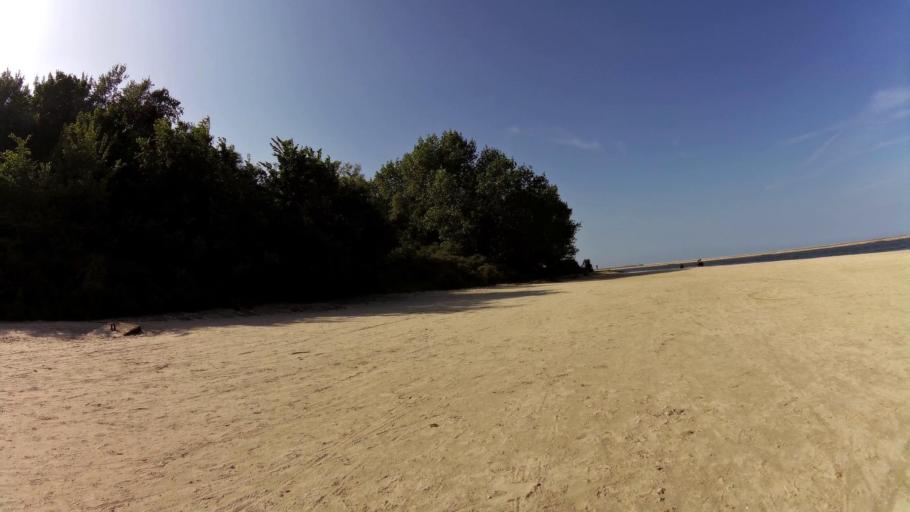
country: PL
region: West Pomeranian Voivodeship
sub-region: Swinoujscie
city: Swinoujscie
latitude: 53.9218
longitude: 14.2791
